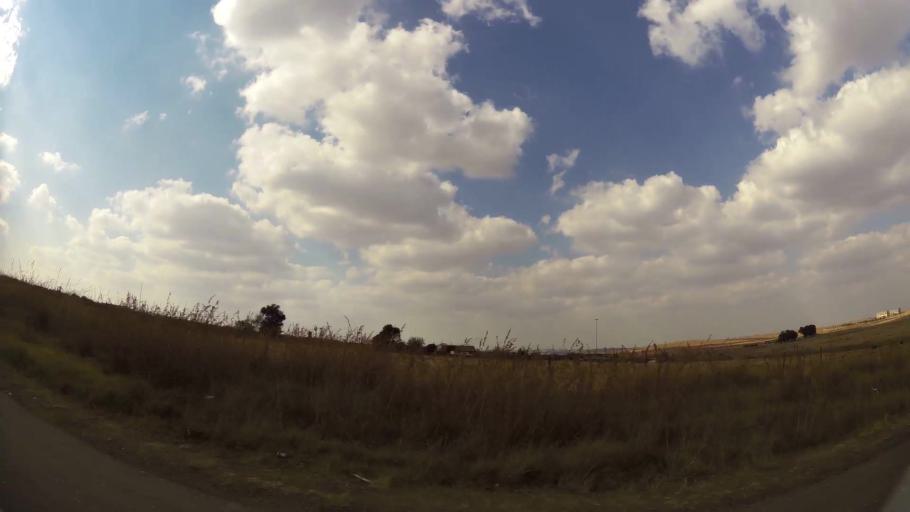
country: ZA
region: Mpumalanga
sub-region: Nkangala District Municipality
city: Delmas
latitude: -26.1061
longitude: 28.6785
